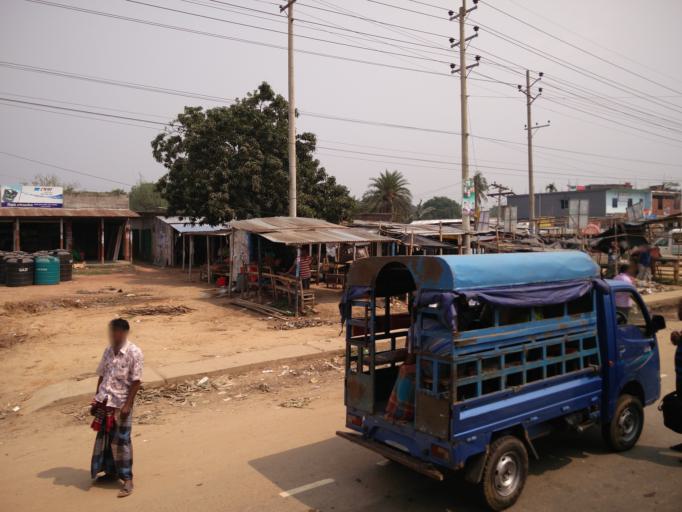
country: BD
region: Dhaka
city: Gafargaon
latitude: 24.4456
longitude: 90.3834
